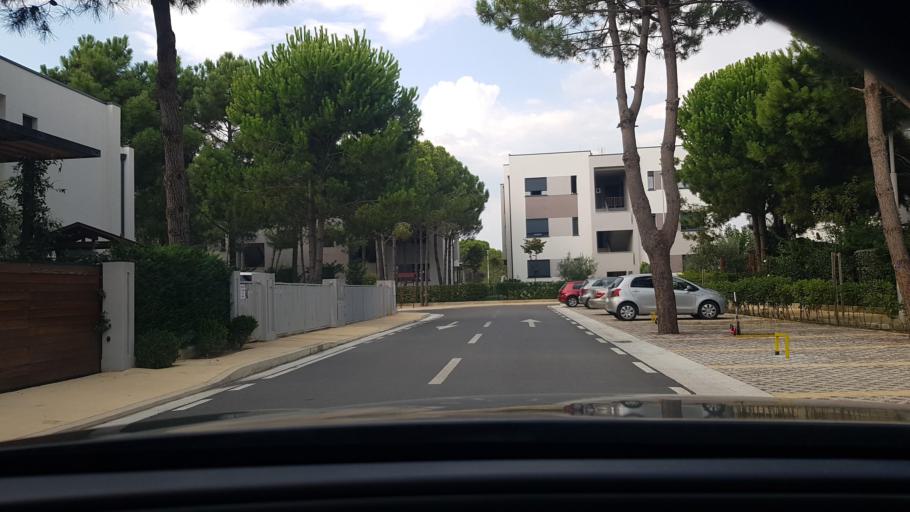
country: AL
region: Durres
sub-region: Rrethi i Durresit
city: Katundi i Ri
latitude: 41.4952
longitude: 19.5152
